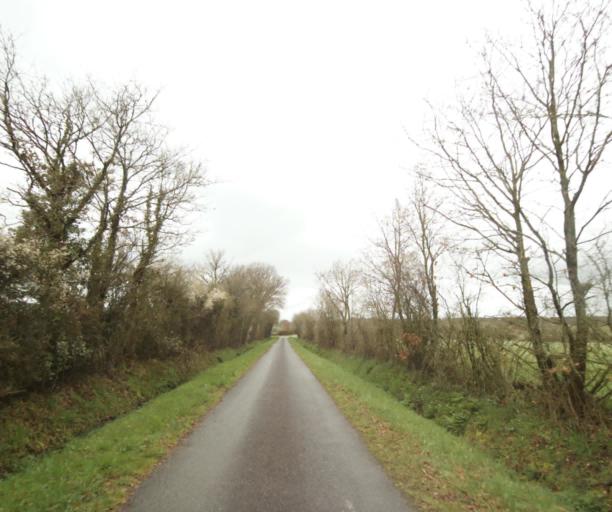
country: FR
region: Pays de la Loire
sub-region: Departement de la Loire-Atlantique
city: Quilly
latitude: 47.4586
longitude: -1.9012
